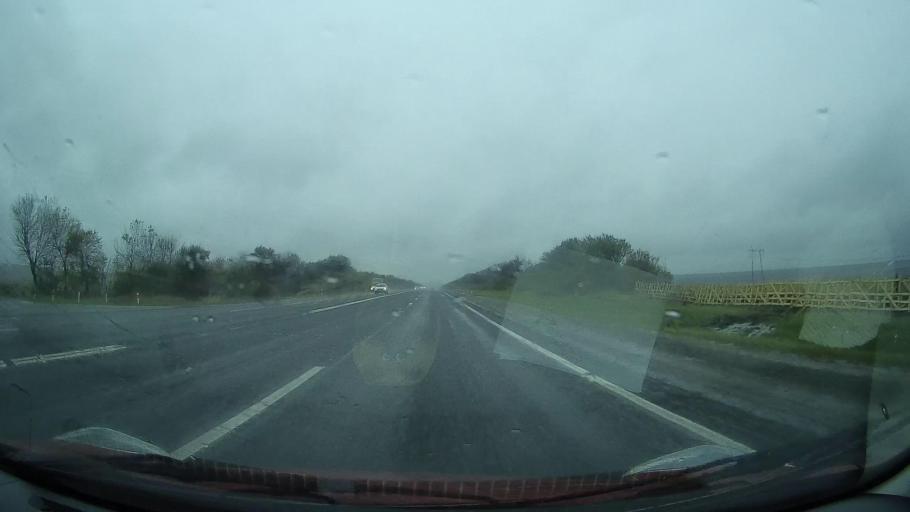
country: RU
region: Stavropol'skiy
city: Nevinnomyssk
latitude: 44.6152
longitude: 42.1083
